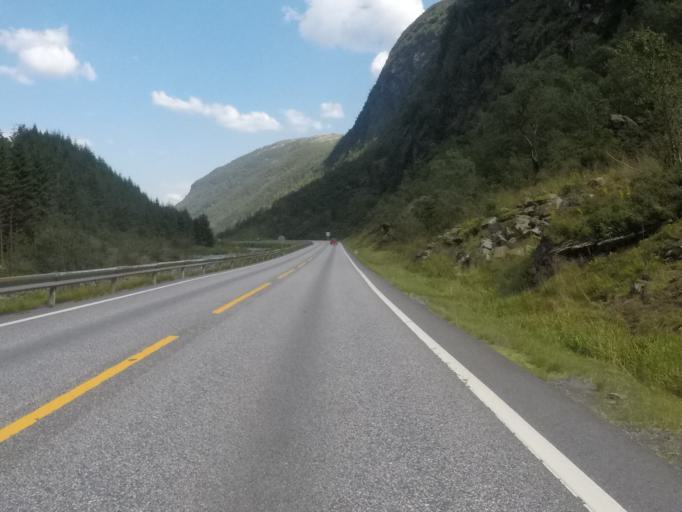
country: NO
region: Hordaland
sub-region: Masfjorden
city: Masfjorden
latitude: 60.9691
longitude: 5.4864
